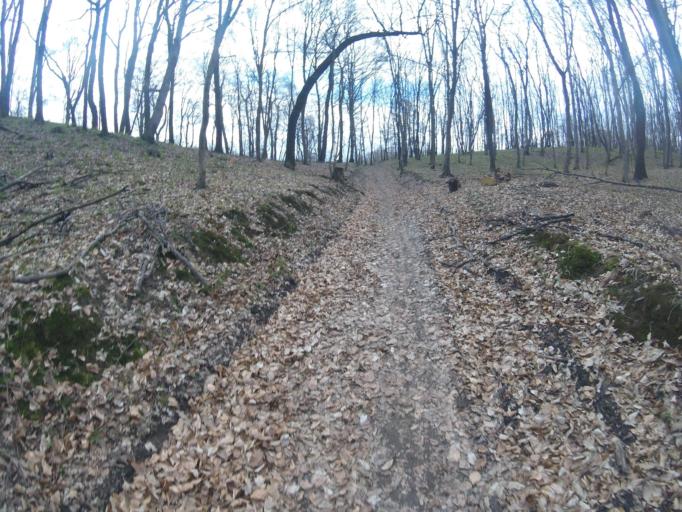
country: HU
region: Fejer
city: Csakvar
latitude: 47.4542
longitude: 18.4059
